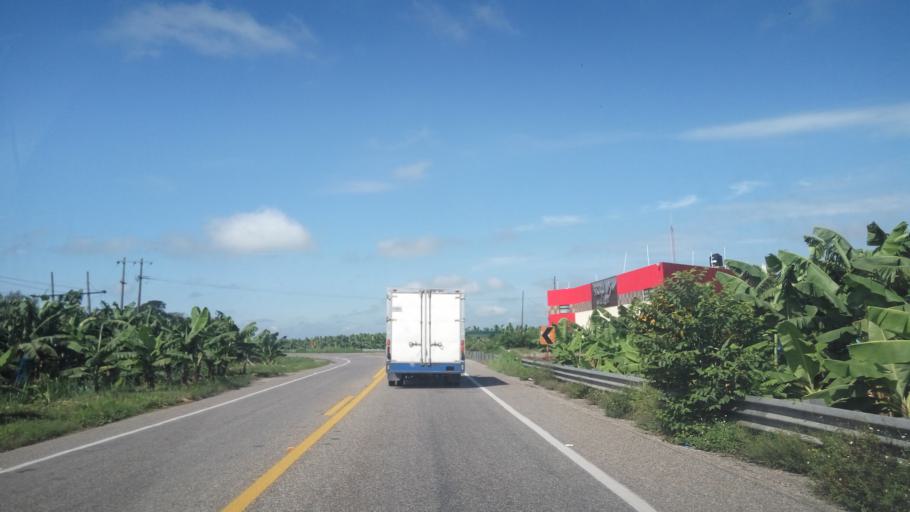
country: MX
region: Tabasco
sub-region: Teapa
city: Eureka y Belen
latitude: 17.6526
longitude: -92.9623
